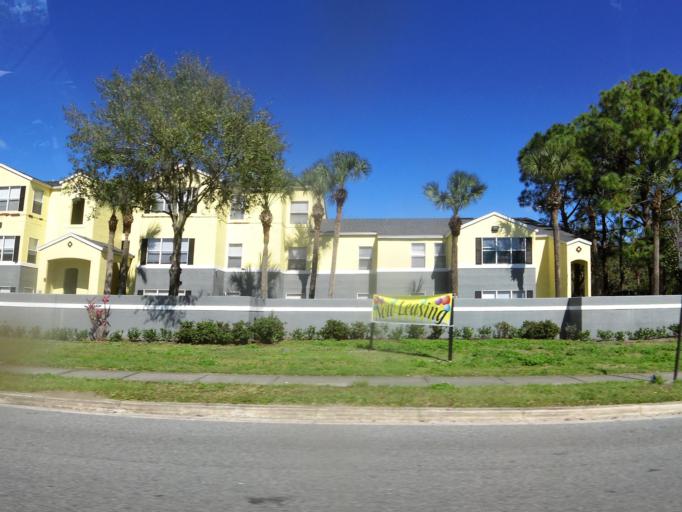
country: US
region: Florida
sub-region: Seminole County
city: Sanford
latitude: 28.8117
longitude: -81.2882
